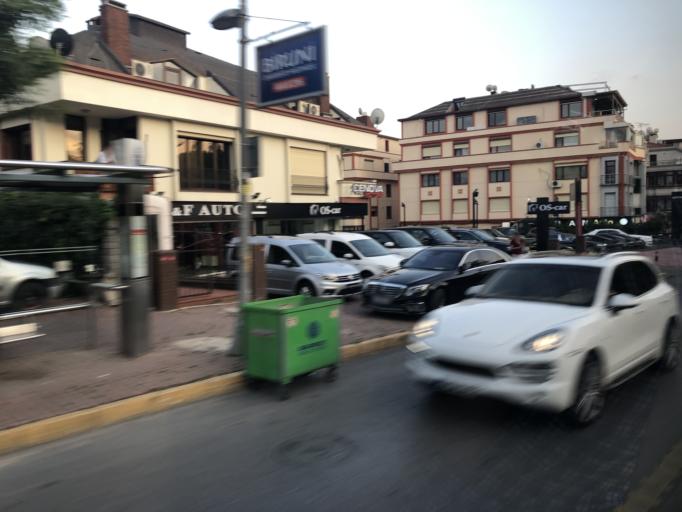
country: TR
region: Istanbul
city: Bahcelievler
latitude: 40.9781
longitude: 28.7919
